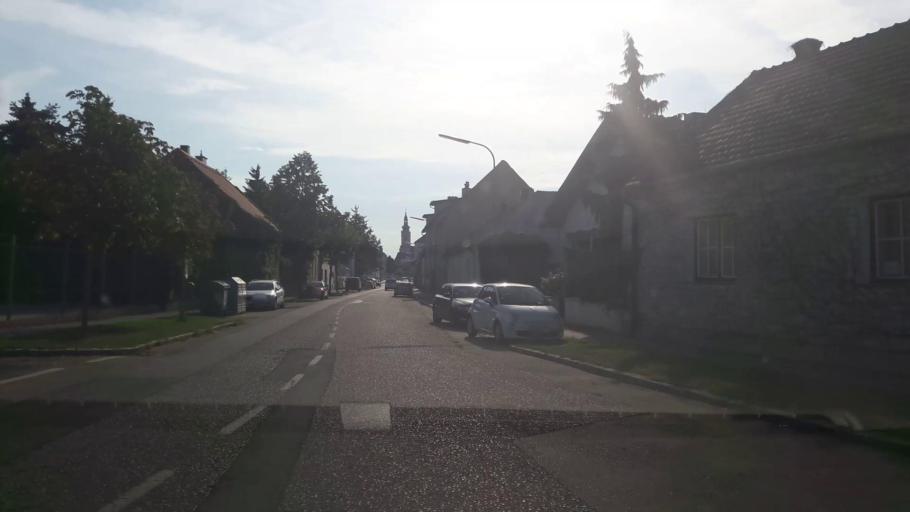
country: AT
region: Lower Austria
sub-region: Politischer Bezirk Bruck an der Leitha
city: Bruck an der Leitha
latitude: 48.0256
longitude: 16.7713
